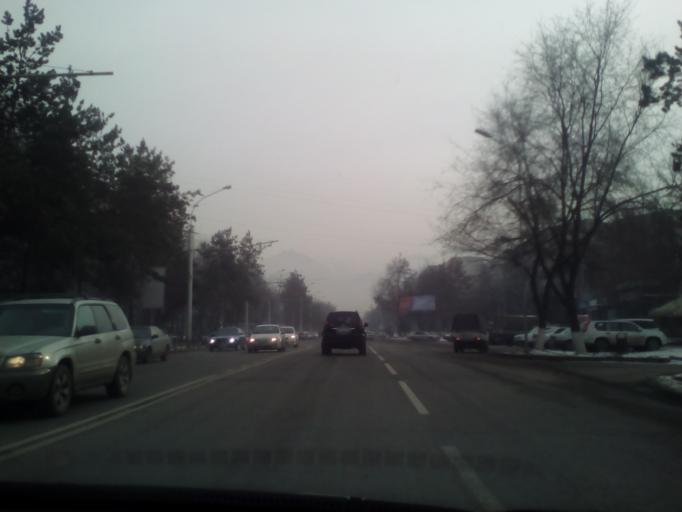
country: KZ
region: Almaty Qalasy
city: Almaty
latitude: 43.2370
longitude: 76.8304
